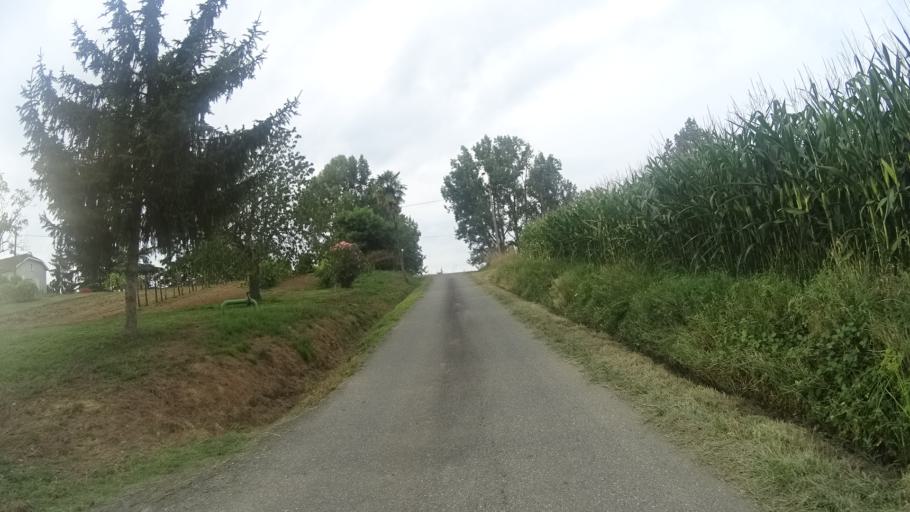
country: FR
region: Aquitaine
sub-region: Departement des Pyrenees-Atlantiques
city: Orthez
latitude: 43.4868
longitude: -0.7078
